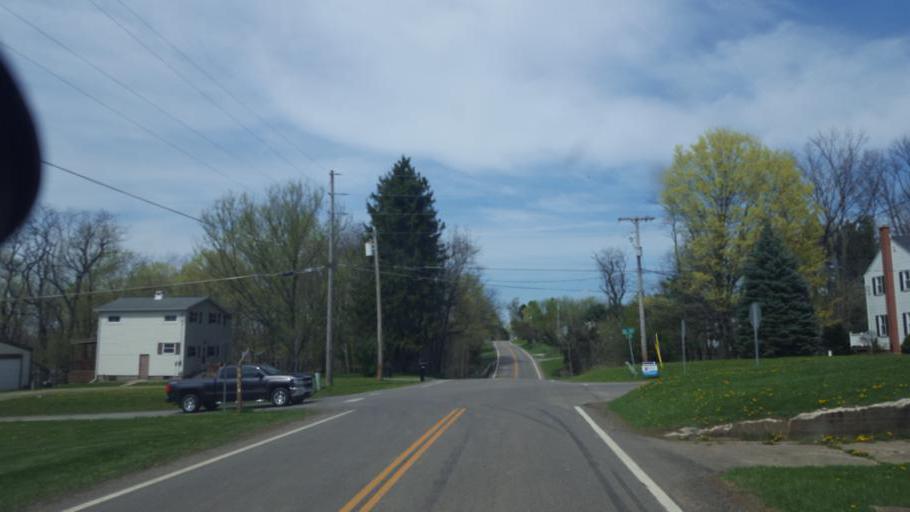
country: US
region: Ohio
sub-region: Ashland County
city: Ashland
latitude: 40.8510
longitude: -82.4025
